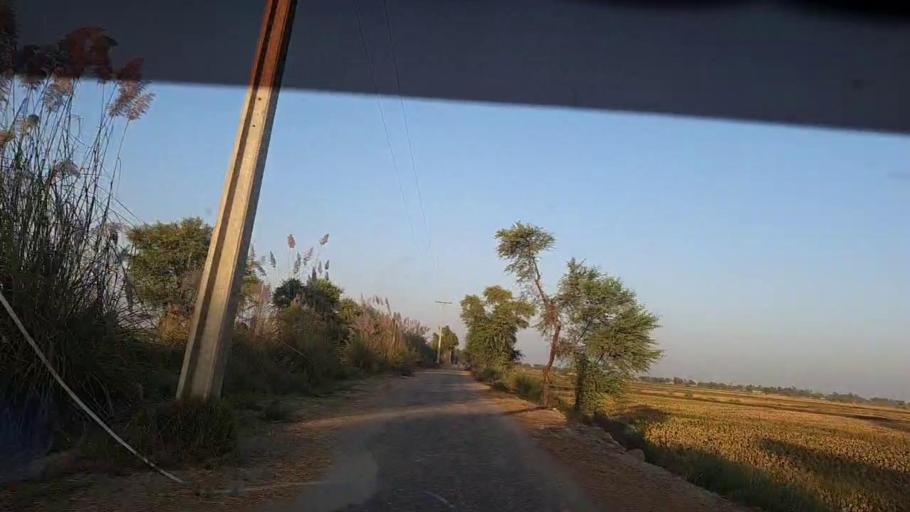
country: PK
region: Sindh
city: Ratodero
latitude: 27.8971
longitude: 68.2287
